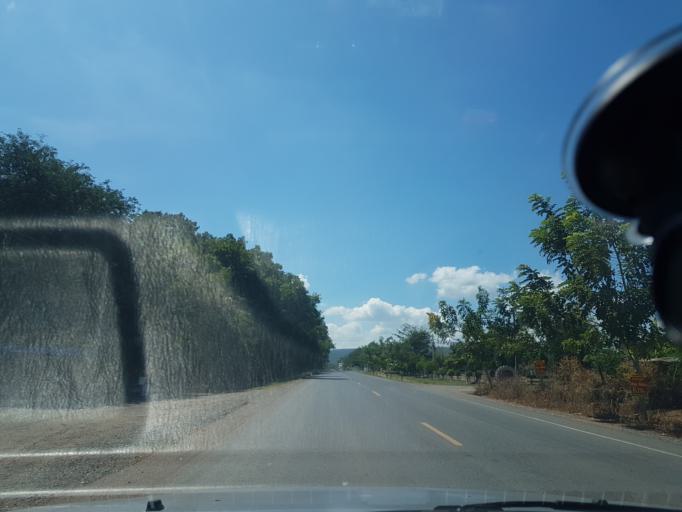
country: TH
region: Lop Buri
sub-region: Amphoe Tha Luang
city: Tha Luang
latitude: 14.9858
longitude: 101.0129
